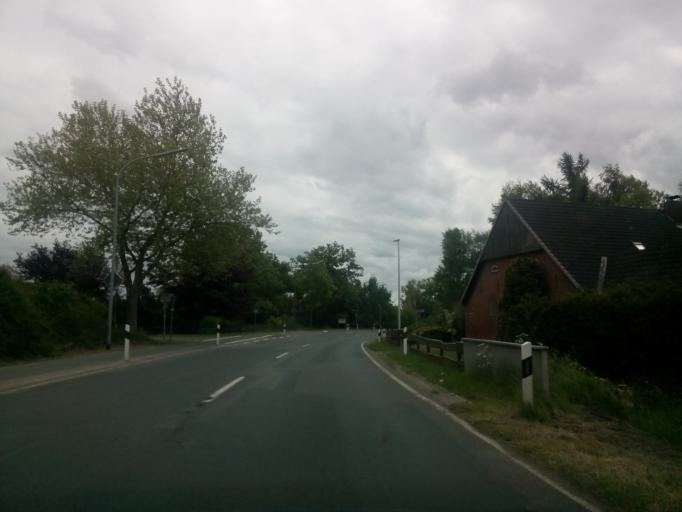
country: DE
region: Lower Saxony
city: Delmenhorst
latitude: 53.1028
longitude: 8.6453
